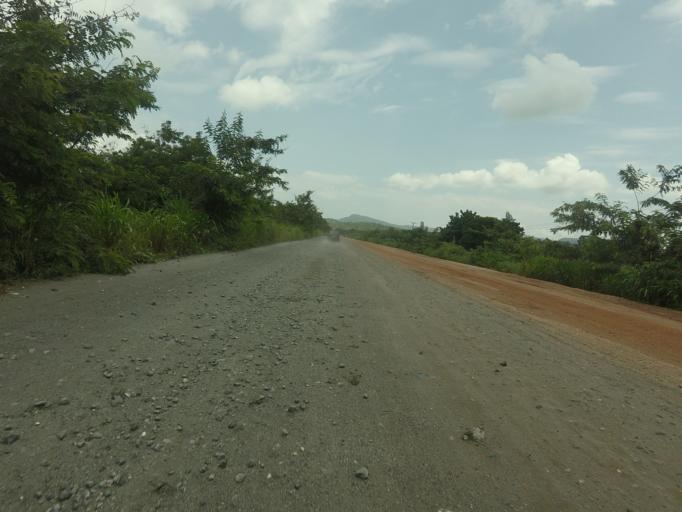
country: GH
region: Volta
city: Ho
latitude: 6.6796
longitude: 0.3221
